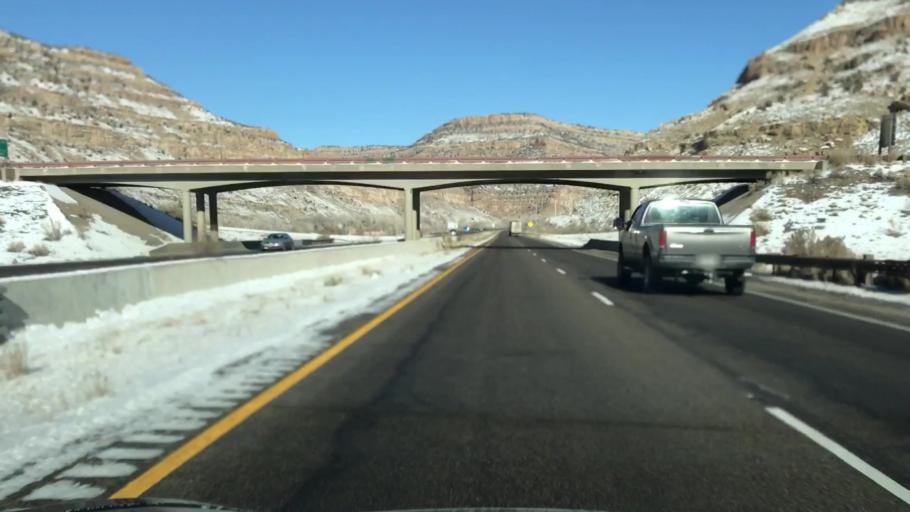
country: US
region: Colorado
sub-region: Mesa County
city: Palisade
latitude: 39.1595
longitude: -108.3006
